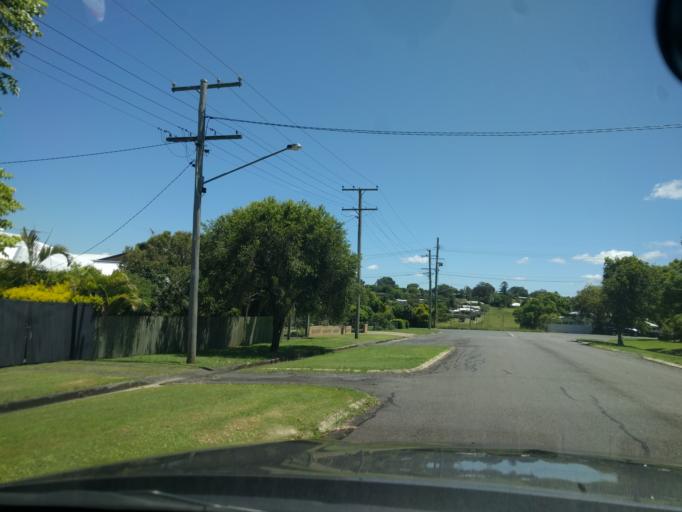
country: AU
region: Queensland
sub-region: Logan
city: Cedar Vale
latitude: -27.9841
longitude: 152.9991
